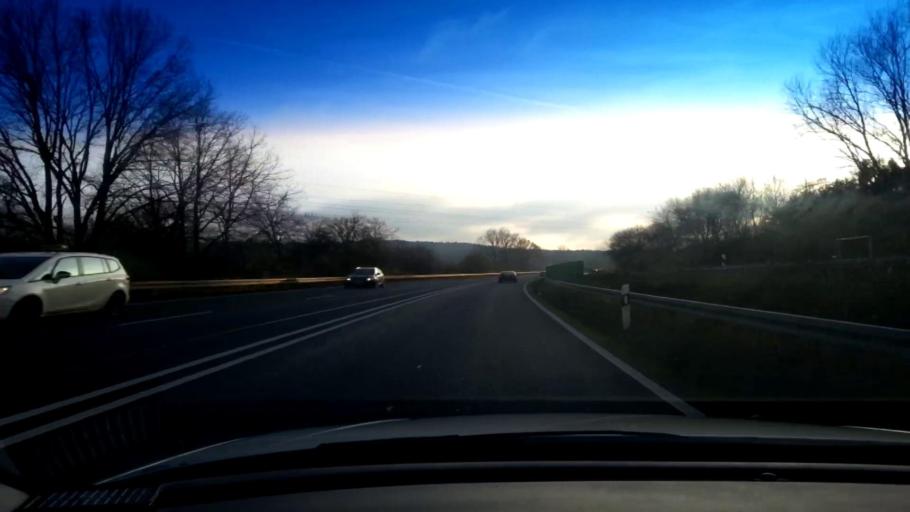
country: DE
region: Bavaria
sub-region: Upper Franconia
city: Hirschaid
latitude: 49.8123
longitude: 10.9644
